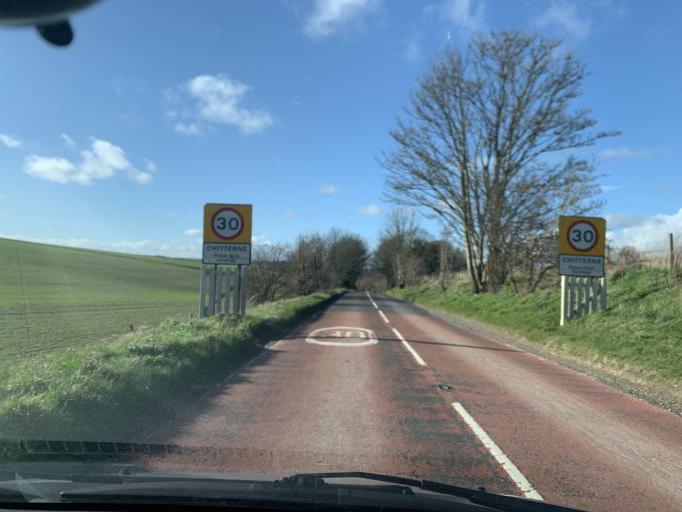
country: GB
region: England
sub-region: Wiltshire
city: Stockton
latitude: 51.1912
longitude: -2.0058
